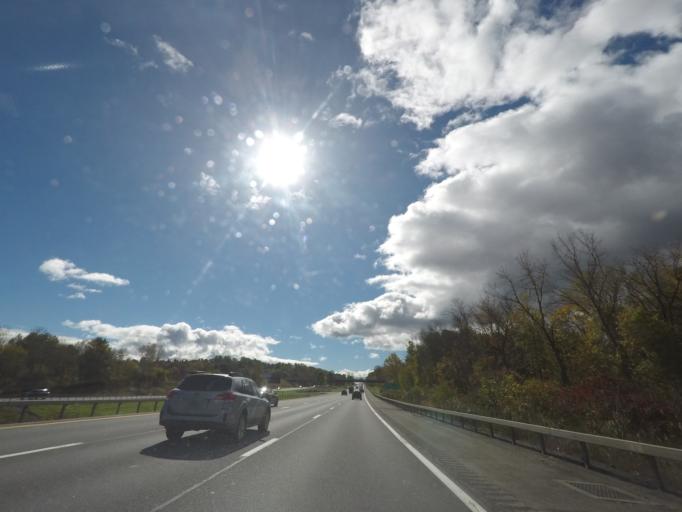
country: US
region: New York
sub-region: Saratoga County
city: Country Knolls
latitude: 42.8928
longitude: -73.7804
